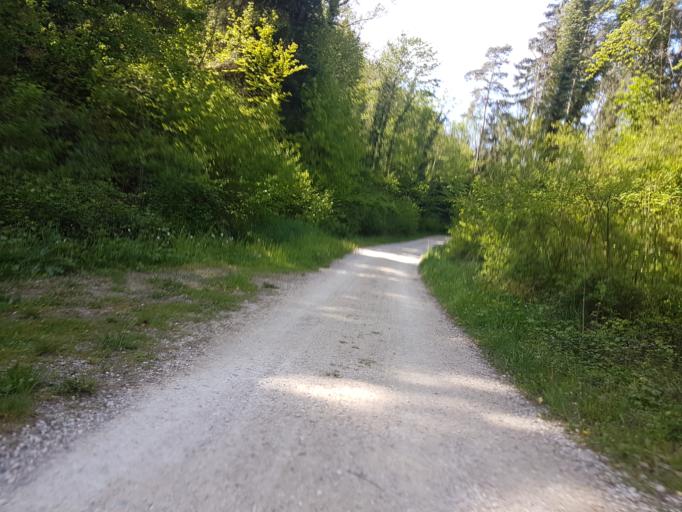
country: CH
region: Bern
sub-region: Seeland District
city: Tauffelen
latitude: 47.0561
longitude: 7.1753
